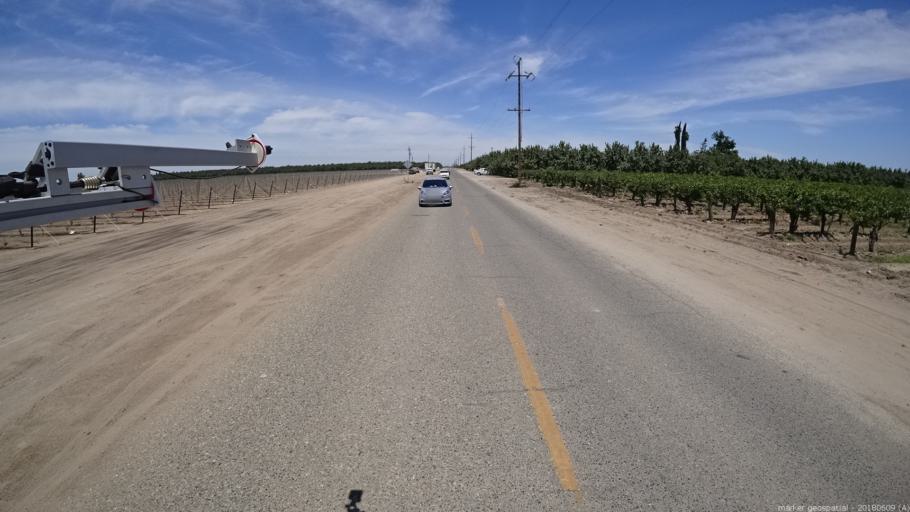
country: US
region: California
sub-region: Madera County
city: Parkwood
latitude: 36.8815
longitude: -120.1104
